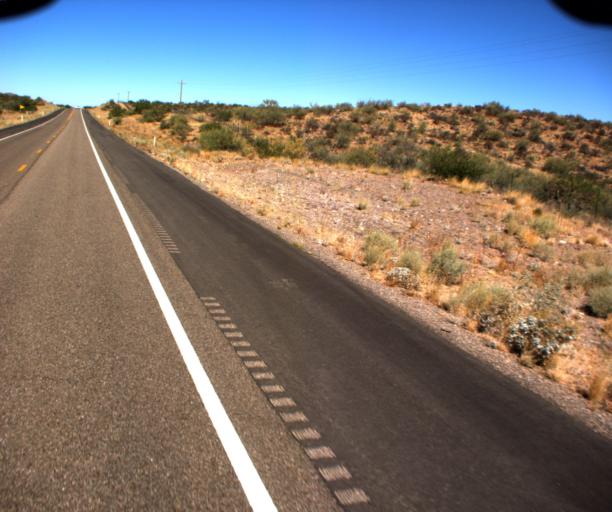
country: US
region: Arizona
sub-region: Pima County
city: Three Points
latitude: 32.0252
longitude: -111.5860
